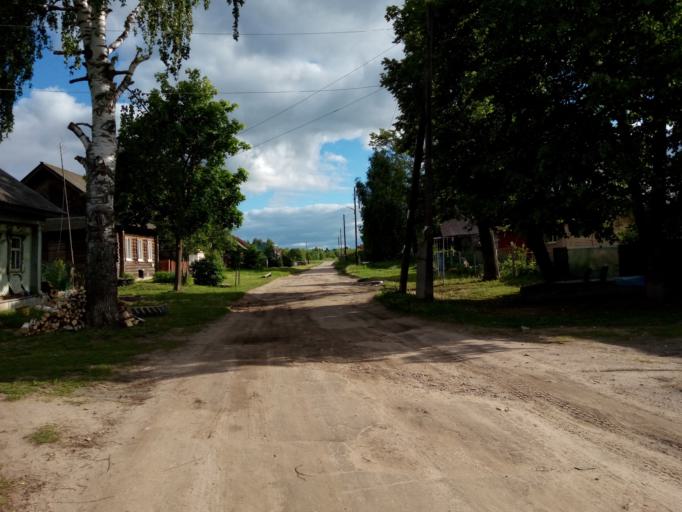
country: RU
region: Nizjnij Novgorod
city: Voskresenskoye
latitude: 56.7831
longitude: 45.5126
